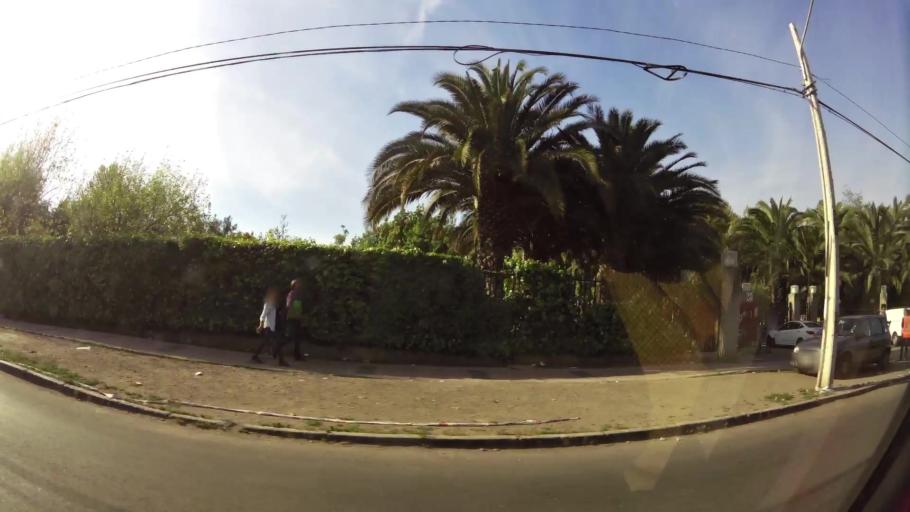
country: CL
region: Santiago Metropolitan
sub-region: Provincia de Santiago
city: Santiago
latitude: -33.5124
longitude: -70.6291
